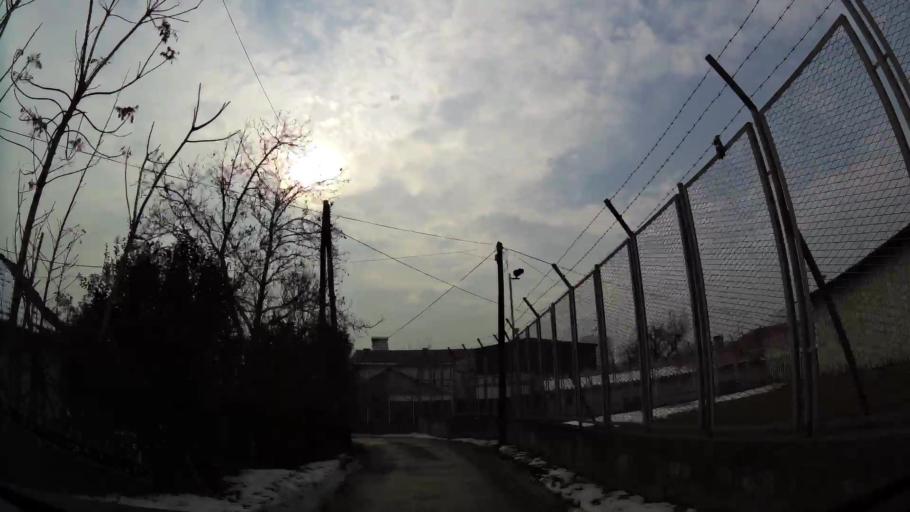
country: MK
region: Karpos
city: Skopje
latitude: 41.9931
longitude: 21.4545
